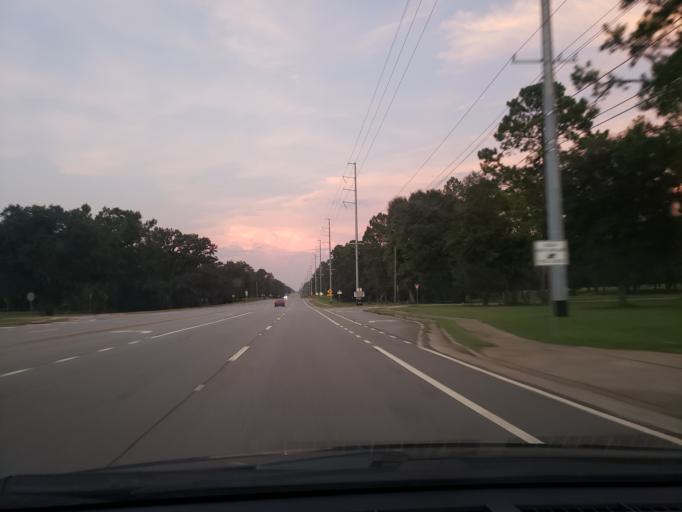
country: US
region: Georgia
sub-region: Dougherty County
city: Albany
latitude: 31.5856
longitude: -84.2752
